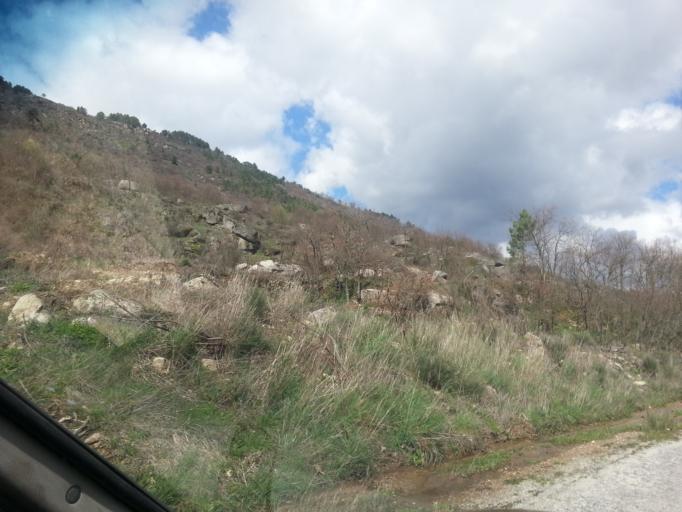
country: PT
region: Guarda
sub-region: Fornos de Algodres
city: Fornos de Algodres
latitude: 40.6462
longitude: -7.5054
